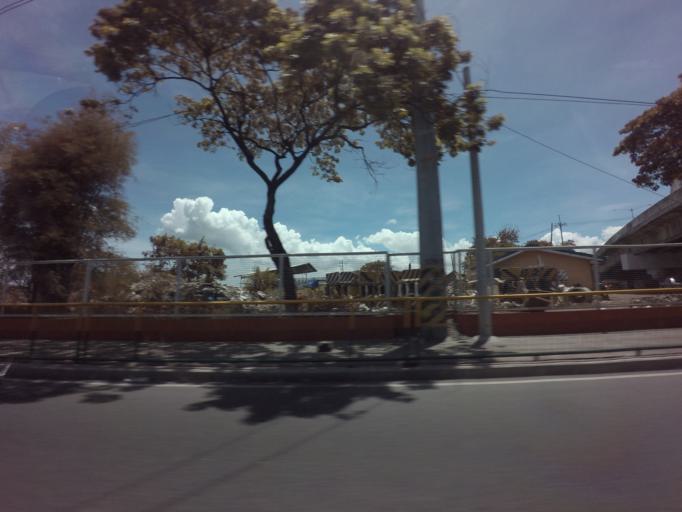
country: PH
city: Sambayanihan People's Village
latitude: 14.4850
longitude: 120.9929
